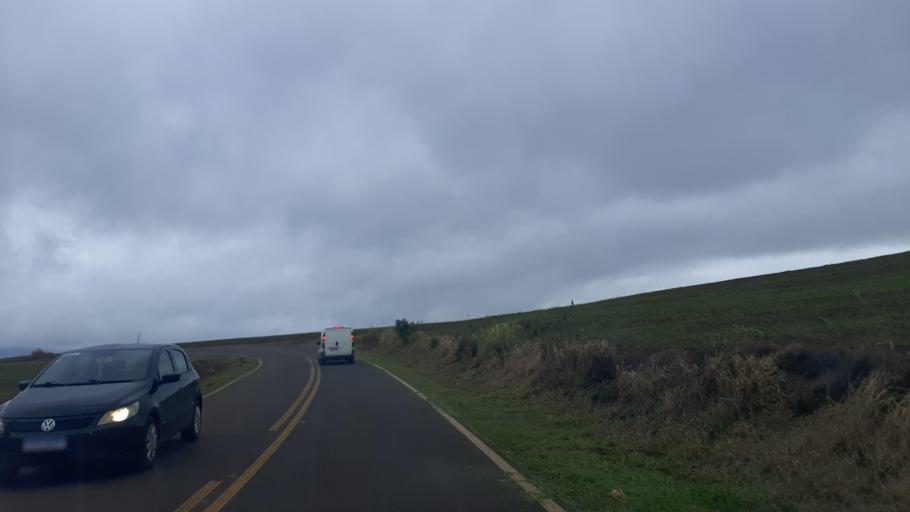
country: BR
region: Parana
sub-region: Ampere
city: Ampere
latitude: -25.9538
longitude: -53.4578
